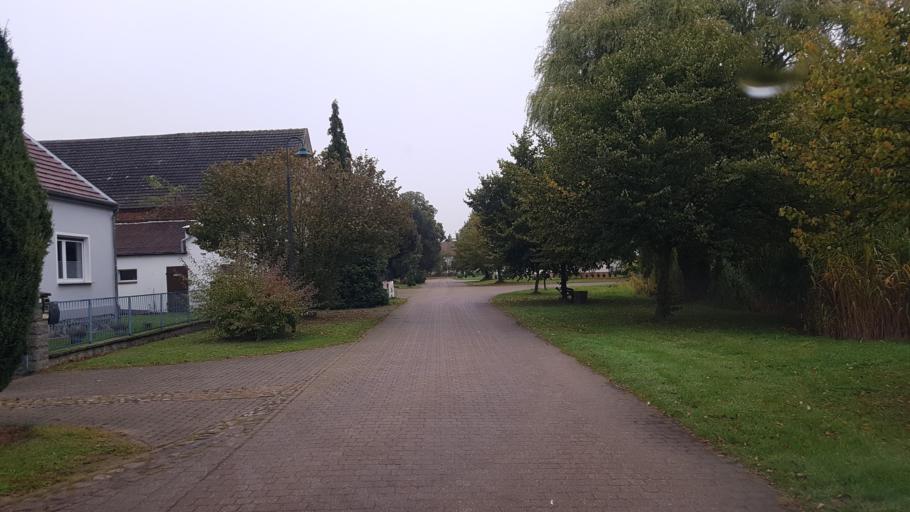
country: DE
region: Brandenburg
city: Furstenwalde
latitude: 52.4344
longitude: 14.0165
